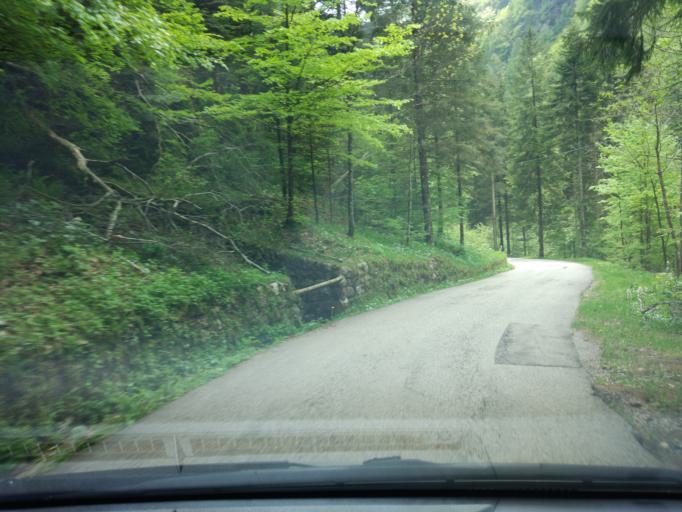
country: IT
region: Veneto
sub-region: Provincia di Verona
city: Selva di Progno
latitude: 45.6811
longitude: 11.1168
